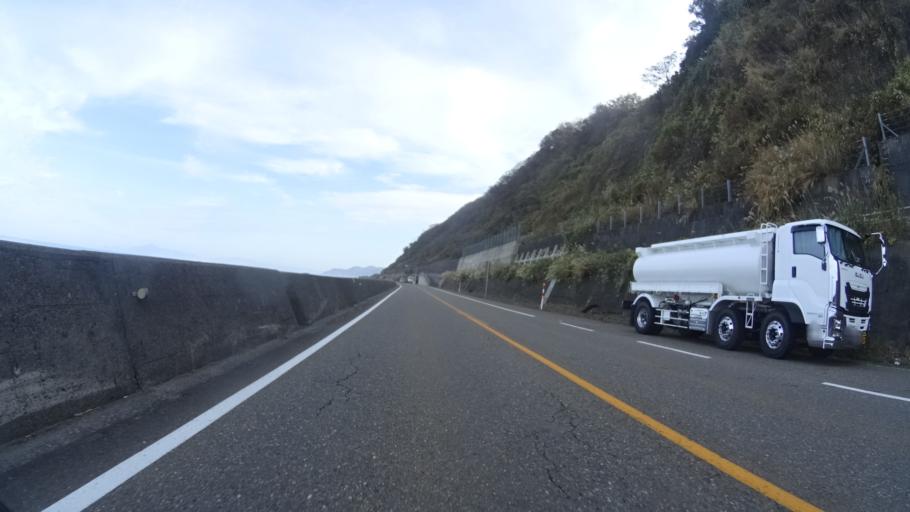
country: JP
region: Niigata
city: Joetsu
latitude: 37.1729
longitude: 138.1043
